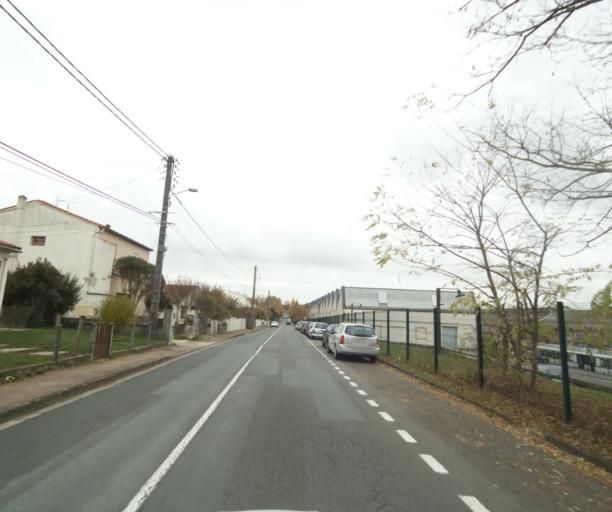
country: FR
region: Poitou-Charentes
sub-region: Departement de la Charente-Maritime
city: Saintes
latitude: 45.7507
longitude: -0.6139
